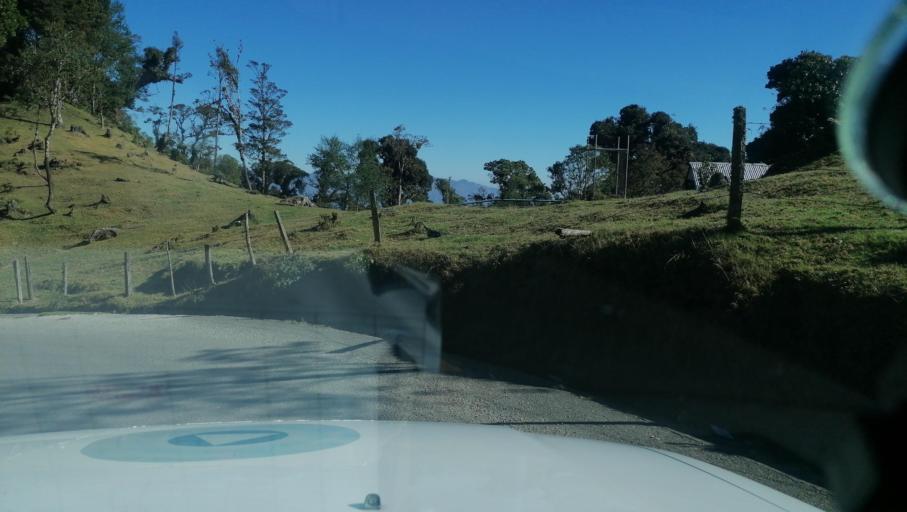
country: MX
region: Chiapas
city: Motozintla de Mendoza
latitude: 15.2650
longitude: -92.2181
